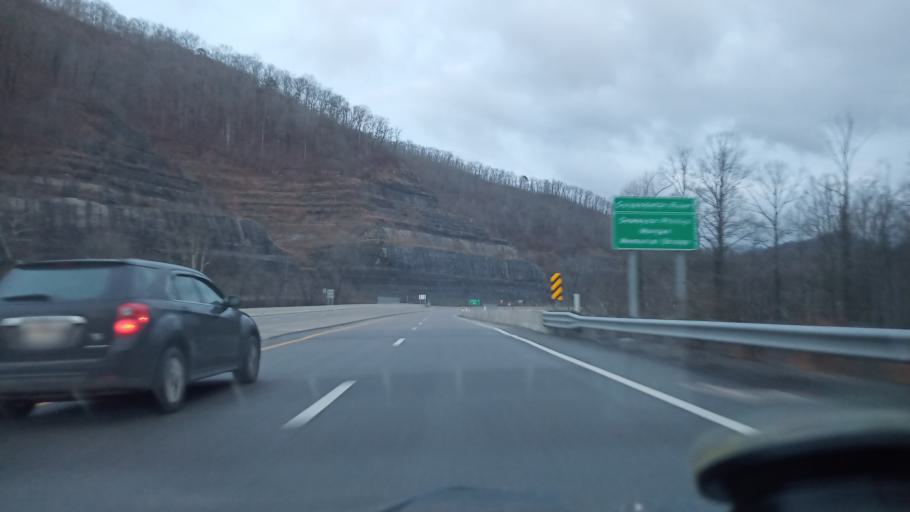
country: US
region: West Virginia
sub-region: Logan County
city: Logan
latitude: 37.7791
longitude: -81.9387
